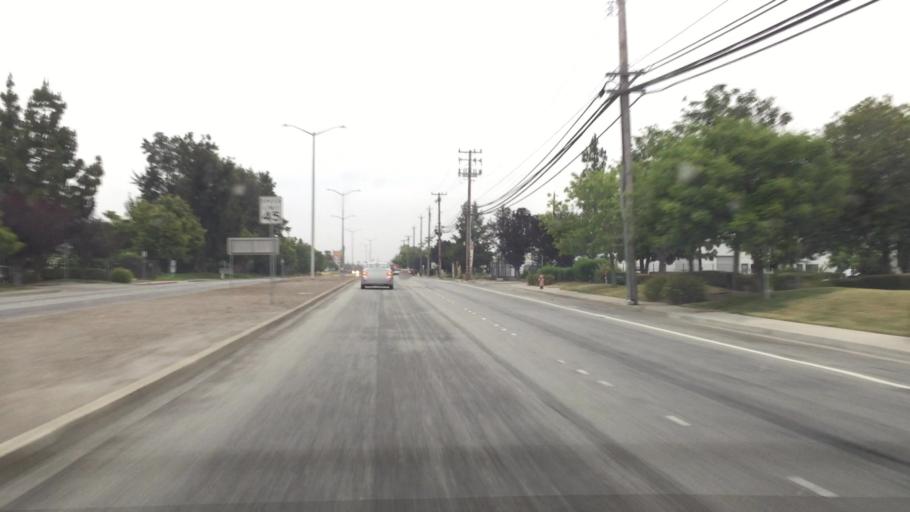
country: US
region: California
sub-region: Alameda County
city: Fremont
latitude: 37.5075
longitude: -121.9495
